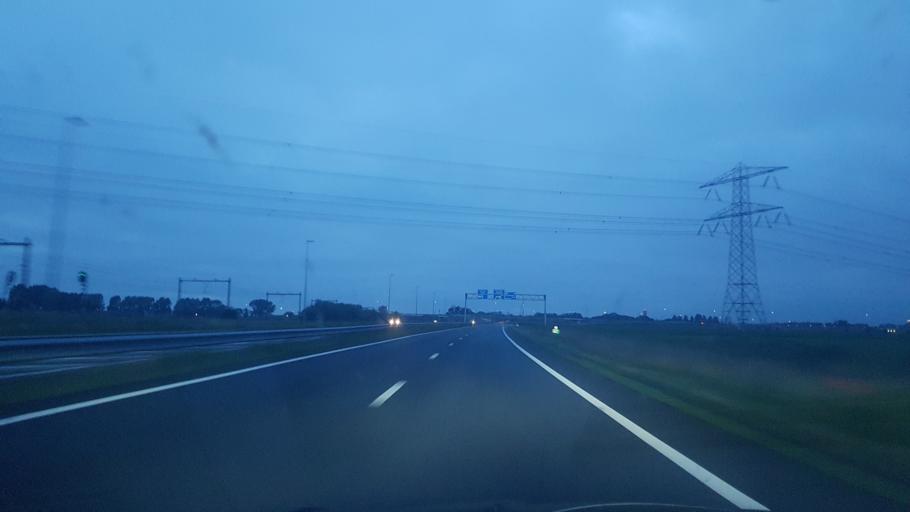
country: NL
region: Friesland
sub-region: Gemeente Leeuwarden
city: Wirdum
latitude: 53.1494
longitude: 5.7936
